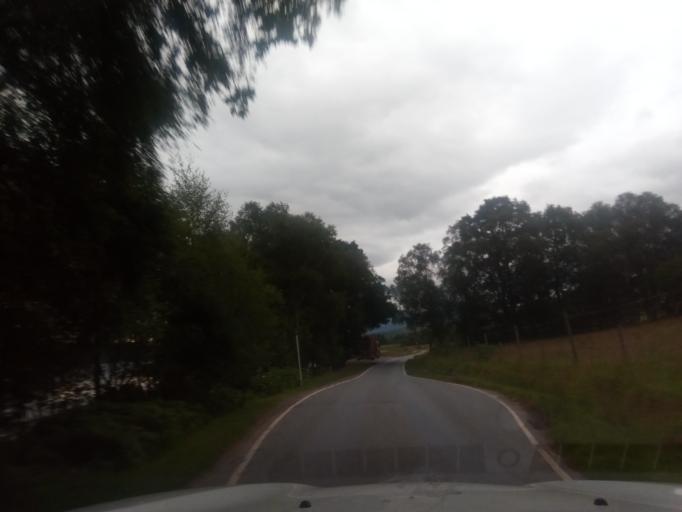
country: GB
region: Scotland
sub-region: Highland
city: Fort William
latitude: 56.8452
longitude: -5.2746
